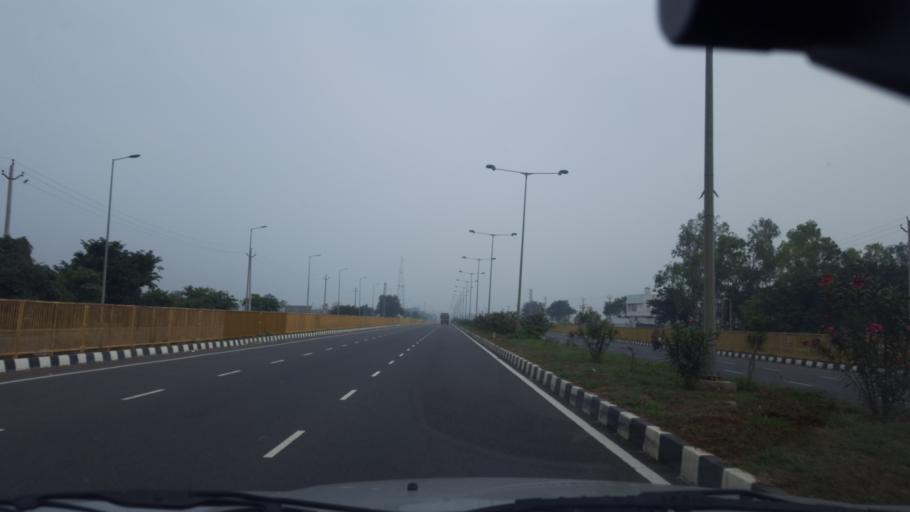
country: IN
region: Andhra Pradesh
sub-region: Prakasam
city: pedda nakkalapalem
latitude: 15.9686
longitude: 80.0948
